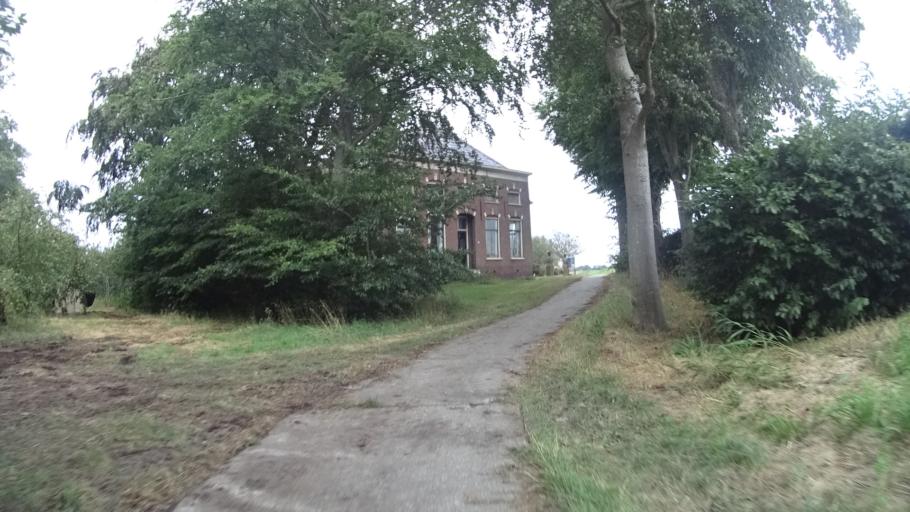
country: NL
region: Groningen
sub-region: Gemeente Hoogezand-Sappemeer
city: Hoogezand
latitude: 53.2354
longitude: 6.7191
